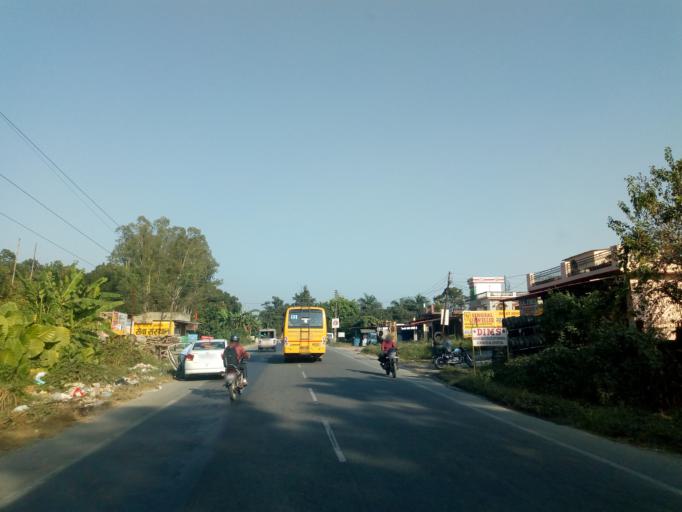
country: IN
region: Uttarakhand
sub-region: Dehradun
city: Dehradun
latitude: 30.3445
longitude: 77.9276
